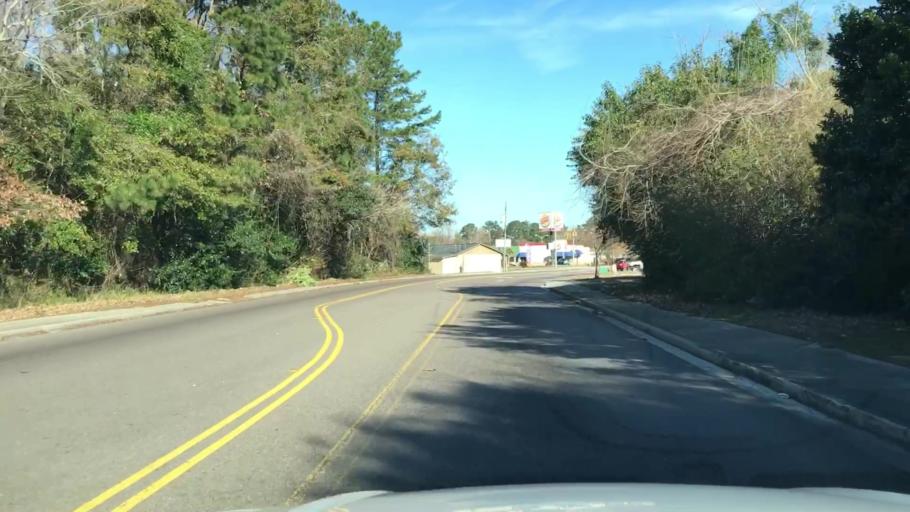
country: US
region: South Carolina
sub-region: Berkeley County
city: Ladson
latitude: 32.9883
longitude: -80.1007
